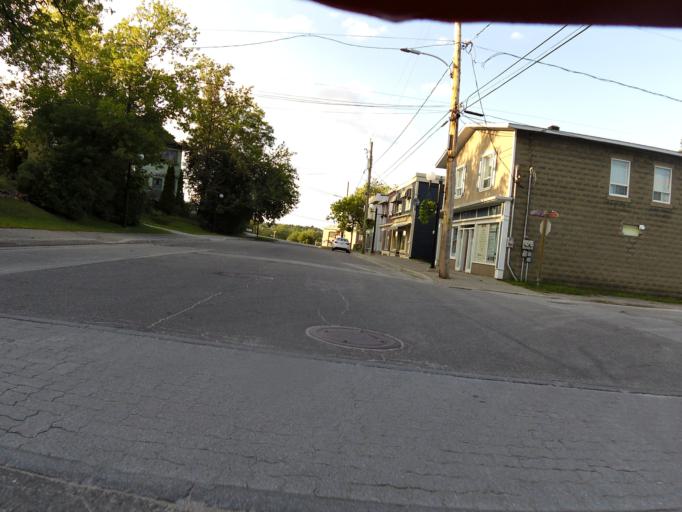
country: CA
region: Quebec
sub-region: Outaouais
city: Maniwaki
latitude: 46.3761
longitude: -75.9766
